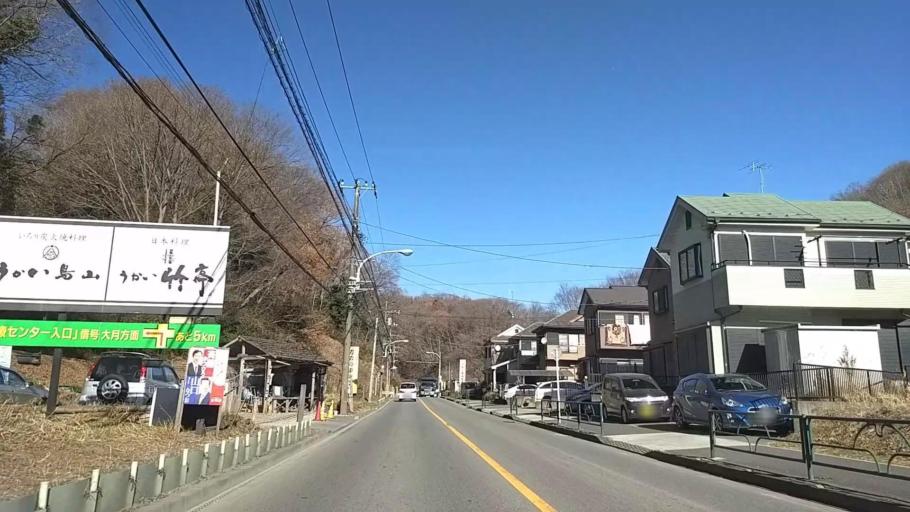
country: JP
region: Tokyo
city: Hachioji
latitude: 35.6148
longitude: 139.2896
